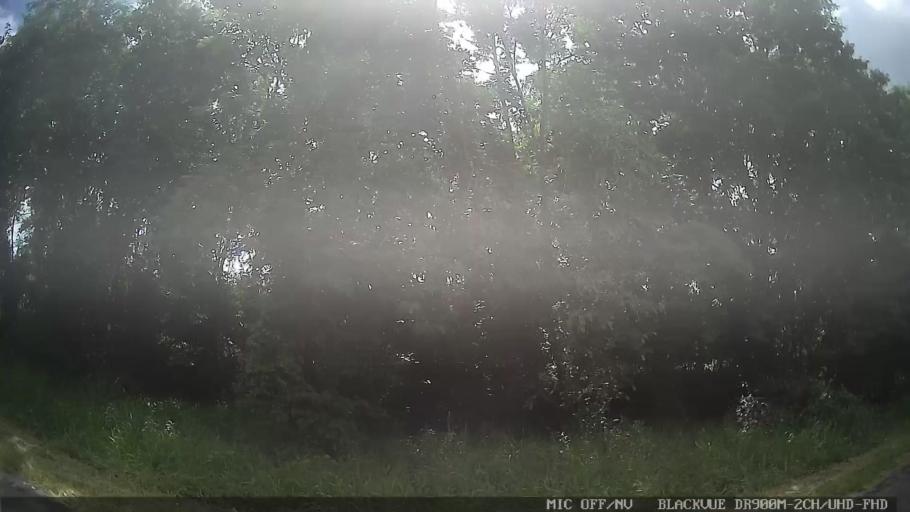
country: BR
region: Sao Paulo
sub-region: Braganca Paulista
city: Braganca Paulista
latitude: -22.8699
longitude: -46.5349
